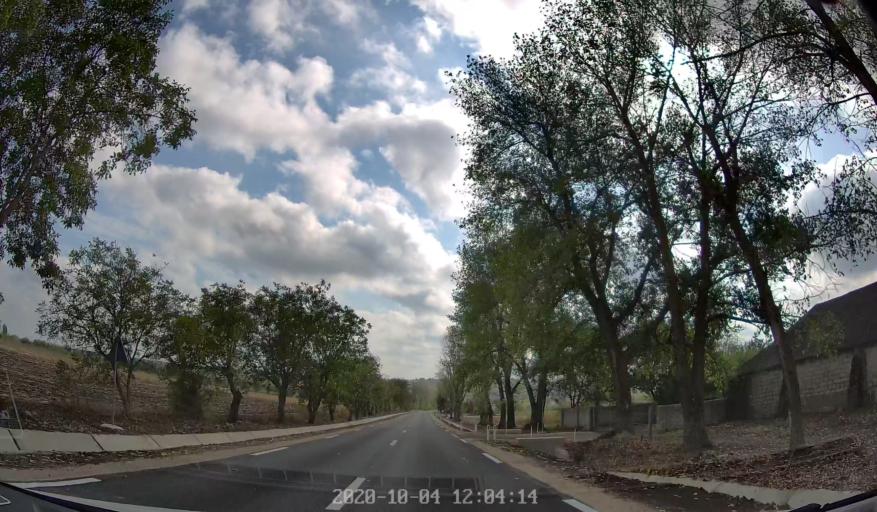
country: MD
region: Rezina
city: Saharna
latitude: 47.6055
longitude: 28.9401
